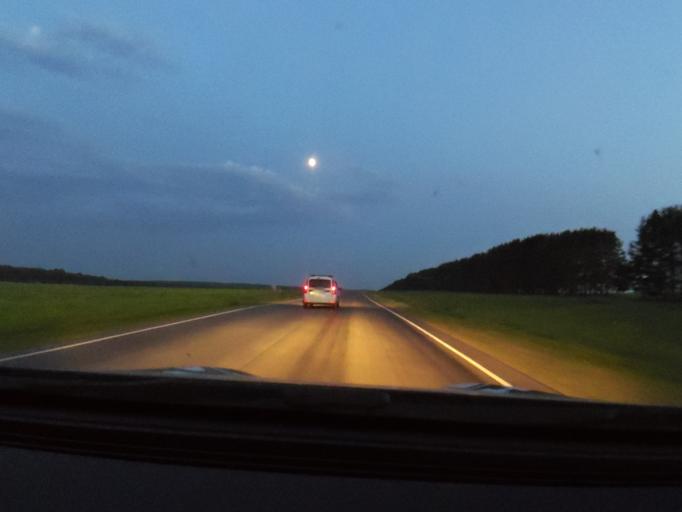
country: RU
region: Bashkortostan
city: Duvan
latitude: 56.0227
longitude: 58.2128
